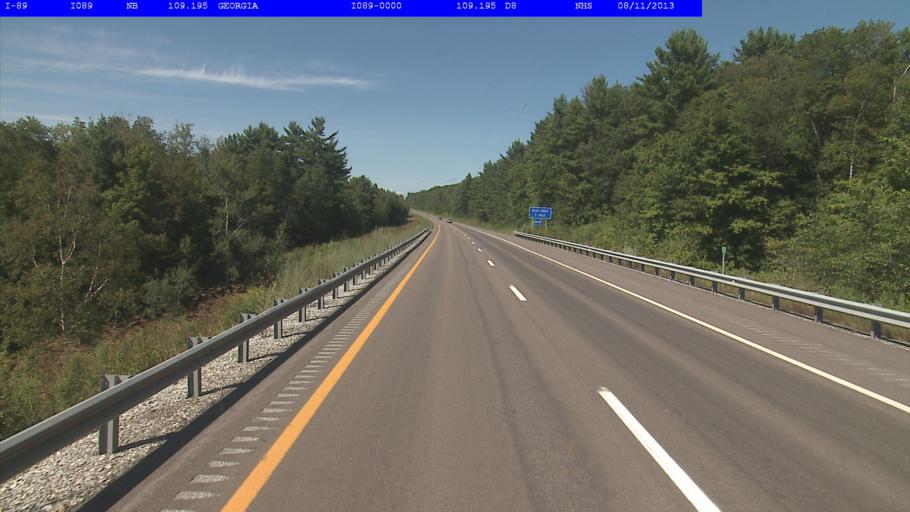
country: US
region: Vermont
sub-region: Franklin County
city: Saint Albans
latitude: 44.7296
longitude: -73.0802
